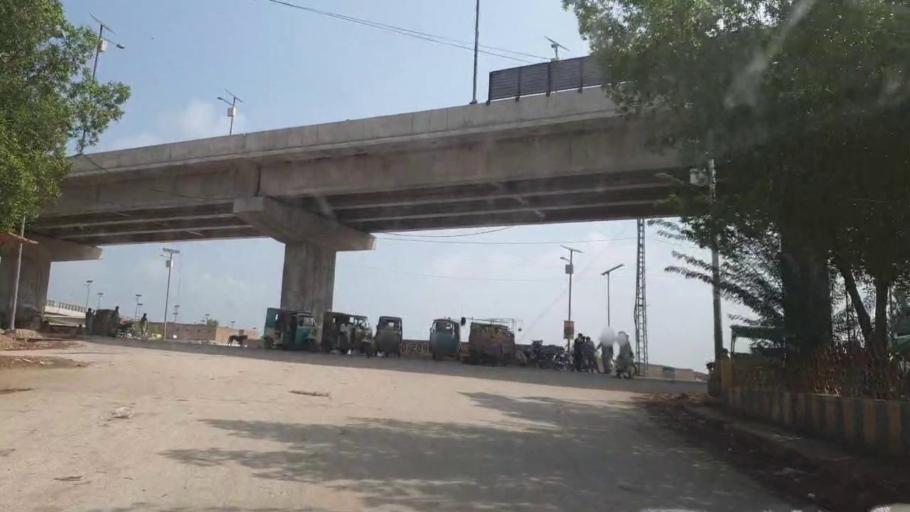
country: PK
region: Sindh
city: Khairpur
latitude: 27.5426
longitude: 68.7569
